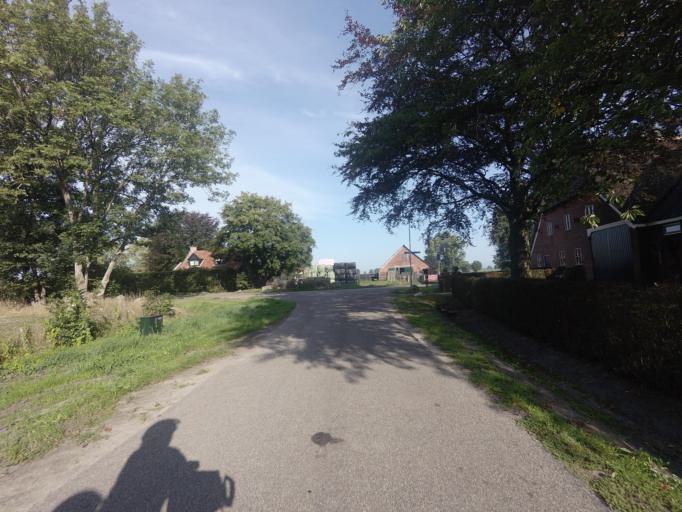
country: NL
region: Groningen
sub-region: Gemeente Leek
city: Leek
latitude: 53.1577
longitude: 6.4329
